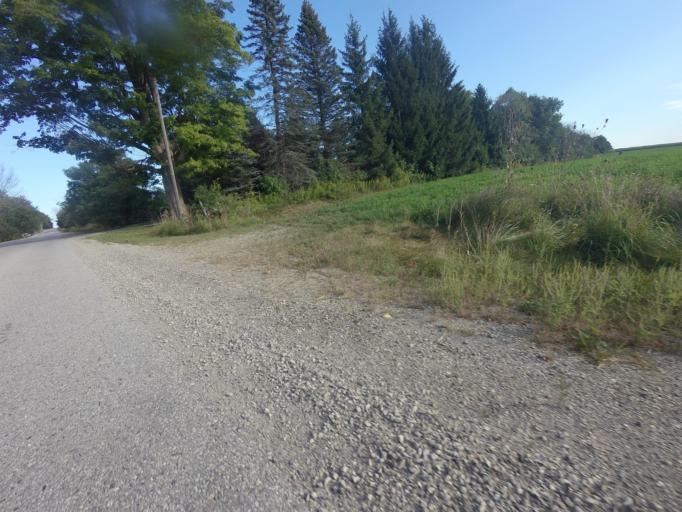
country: CA
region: Ontario
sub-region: Wellington County
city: Guelph
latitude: 43.6128
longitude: -80.3635
